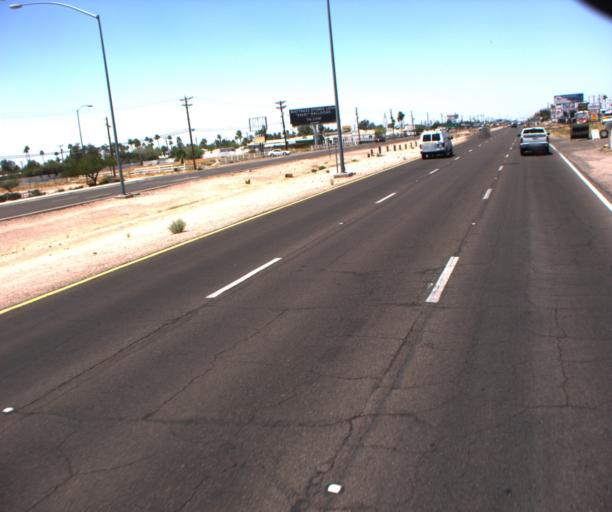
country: US
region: Arizona
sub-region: Pinal County
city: Apache Junction
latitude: 33.4154
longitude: -111.6059
